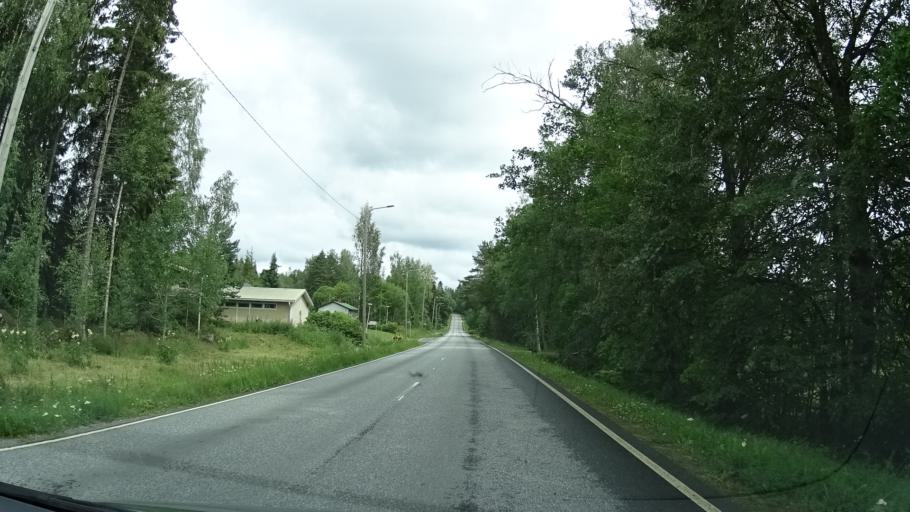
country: FI
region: Pirkanmaa
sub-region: Etelae-Pirkanmaa
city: Urjala
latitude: 61.0839
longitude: 23.4425
